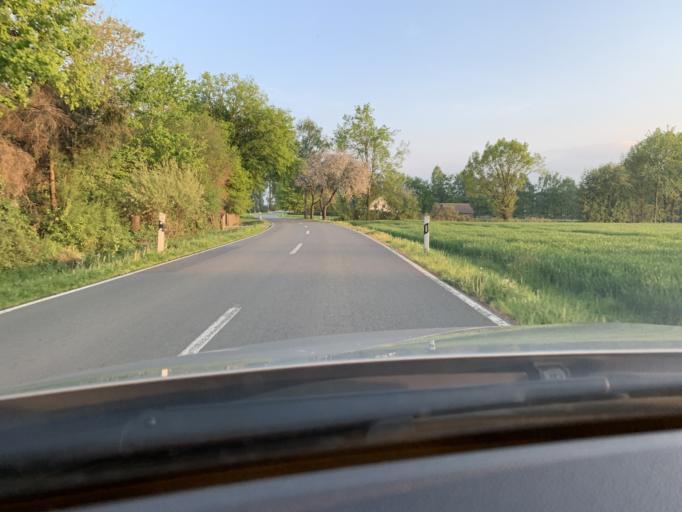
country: DE
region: North Rhine-Westphalia
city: Rietberg
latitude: 51.7846
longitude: 8.4031
